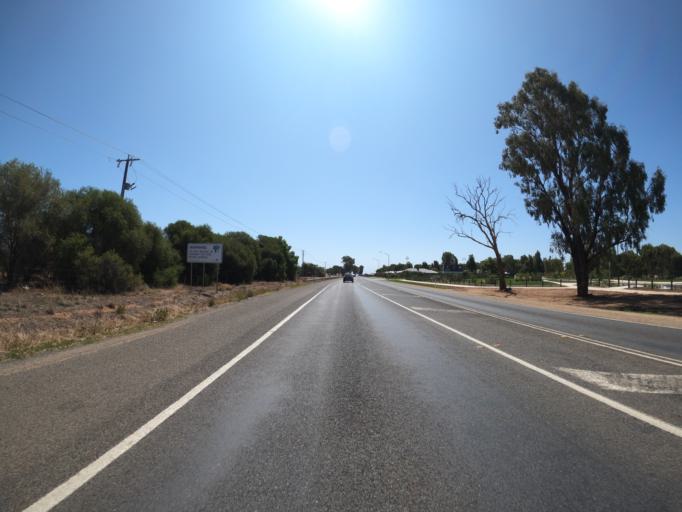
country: AU
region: Victoria
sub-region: Moira
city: Yarrawonga
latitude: -36.0127
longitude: 146.0379
